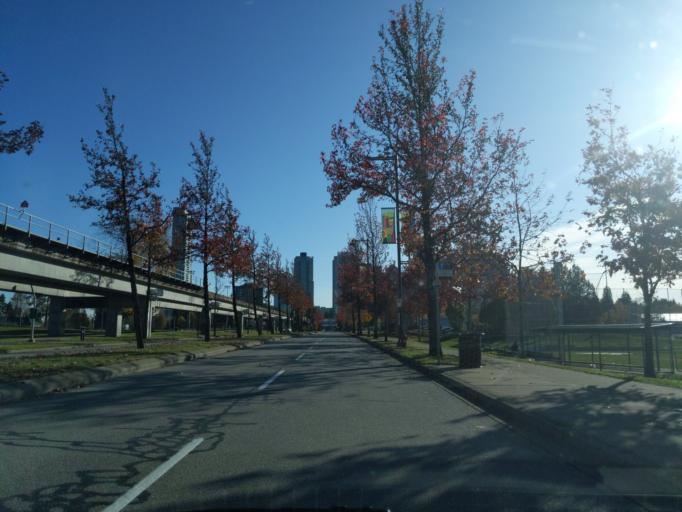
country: CA
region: British Columbia
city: New Westminster
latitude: 49.1973
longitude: -122.8509
